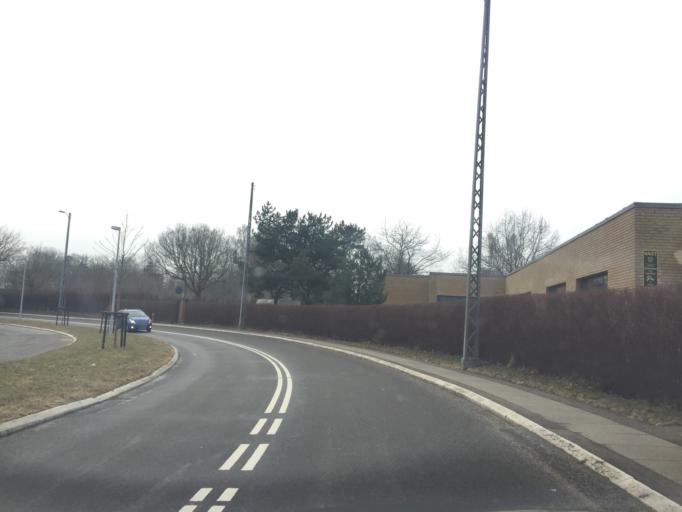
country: DK
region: Capital Region
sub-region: Hoje-Taastrup Kommune
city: Flong
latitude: 55.6495
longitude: 12.2099
